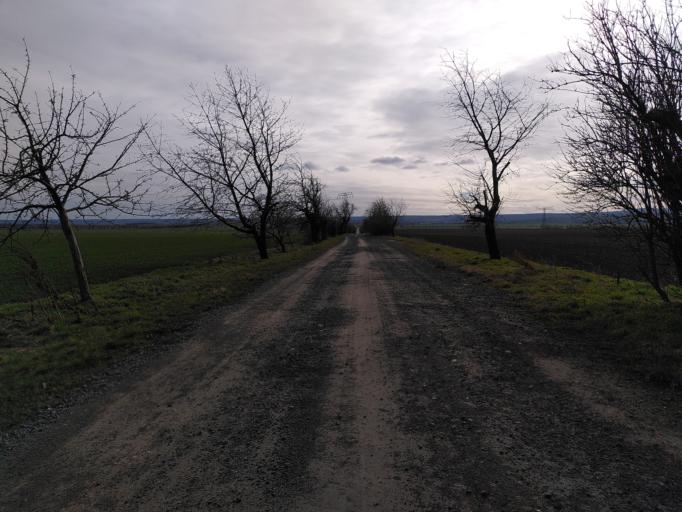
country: DE
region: Saxony-Anhalt
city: Gatersleben
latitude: 51.7971
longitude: 11.2582
